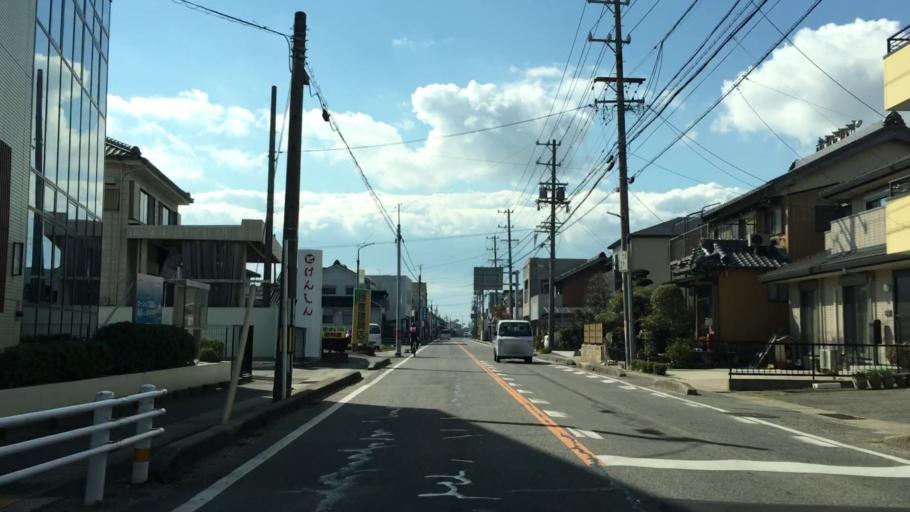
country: JP
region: Aichi
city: Ishiki
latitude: 34.7953
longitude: 137.0668
